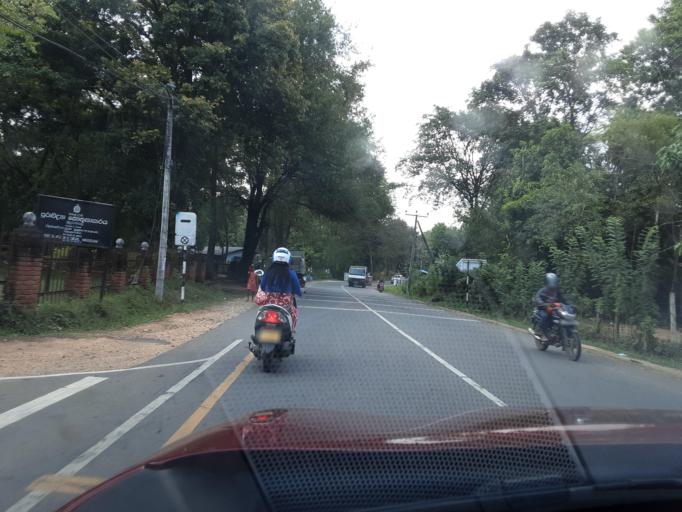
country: LK
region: Uva
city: Haputale
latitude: 6.6903
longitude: 81.1074
